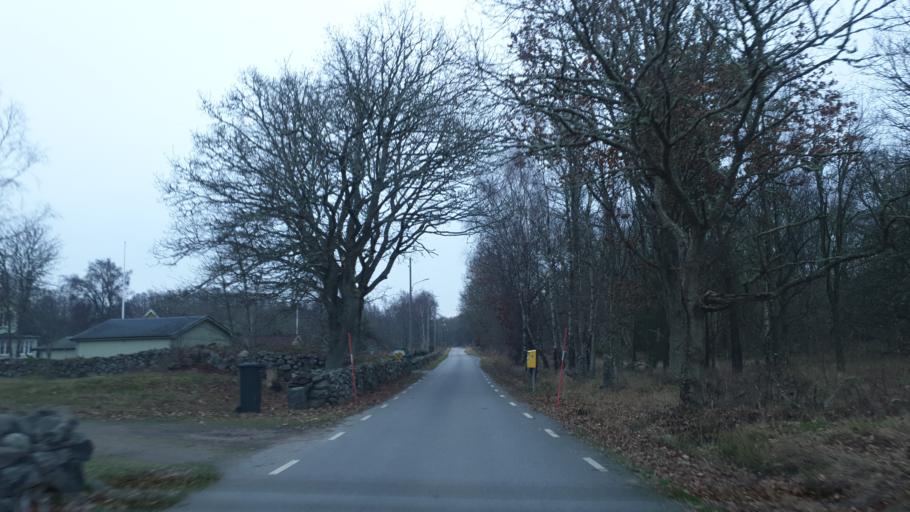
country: SE
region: Blekinge
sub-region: Karlskrona Kommun
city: Karlskrona
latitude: 56.1082
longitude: 15.6116
